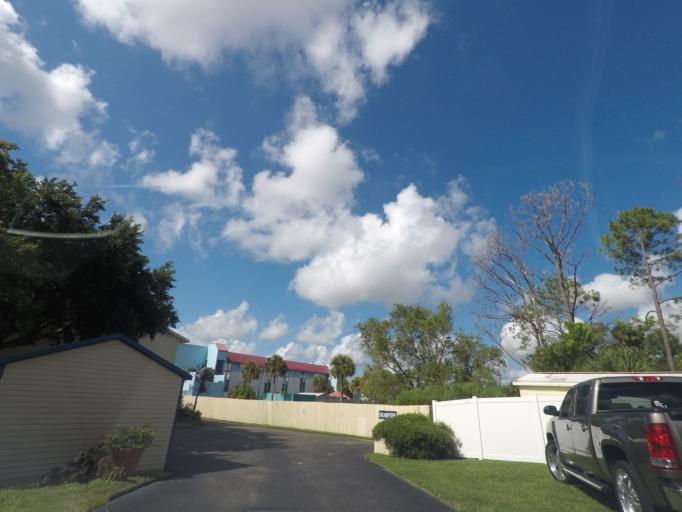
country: US
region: Florida
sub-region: Osceola County
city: Celebration
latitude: 28.3357
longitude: -81.5865
